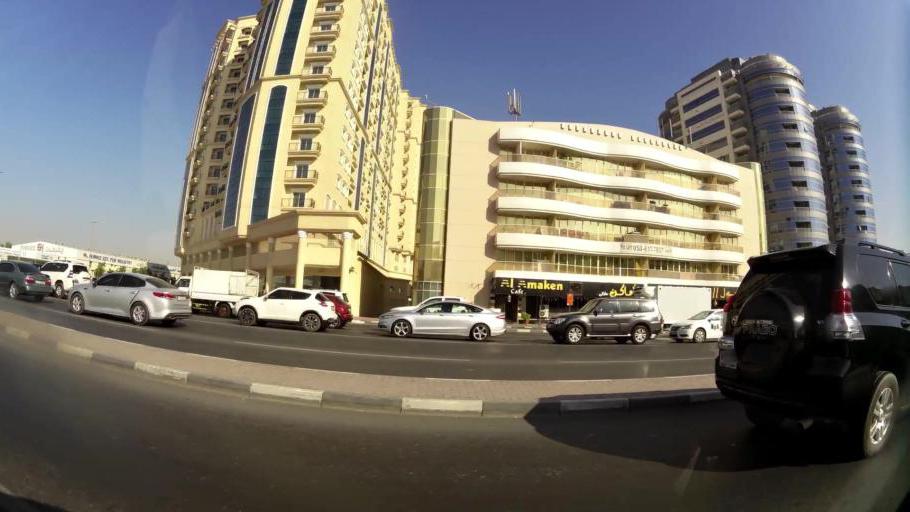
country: AE
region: Ash Shariqah
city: Sharjah
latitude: 25.2928
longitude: 55.3954
